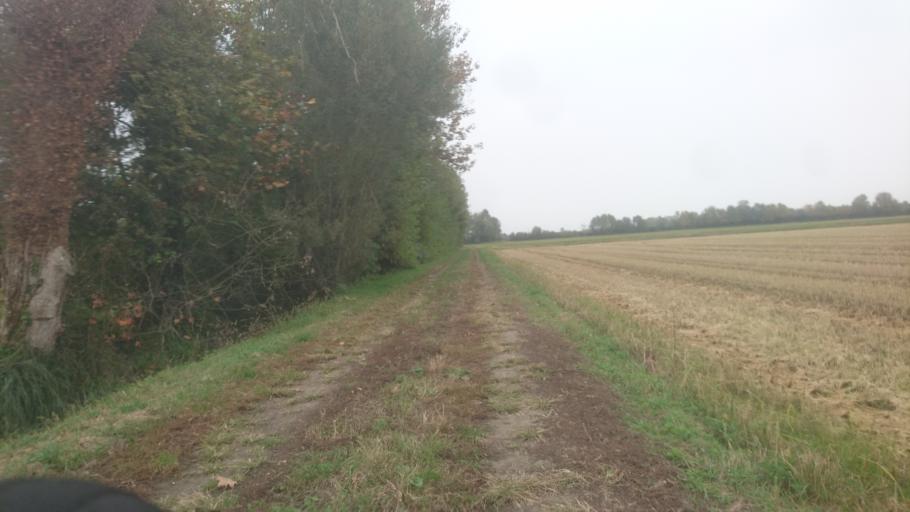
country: IT
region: Veneto
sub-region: Provincia di Vicenza
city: Grumolo delle Abbadesse
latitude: 45.5517
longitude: 11.6709
